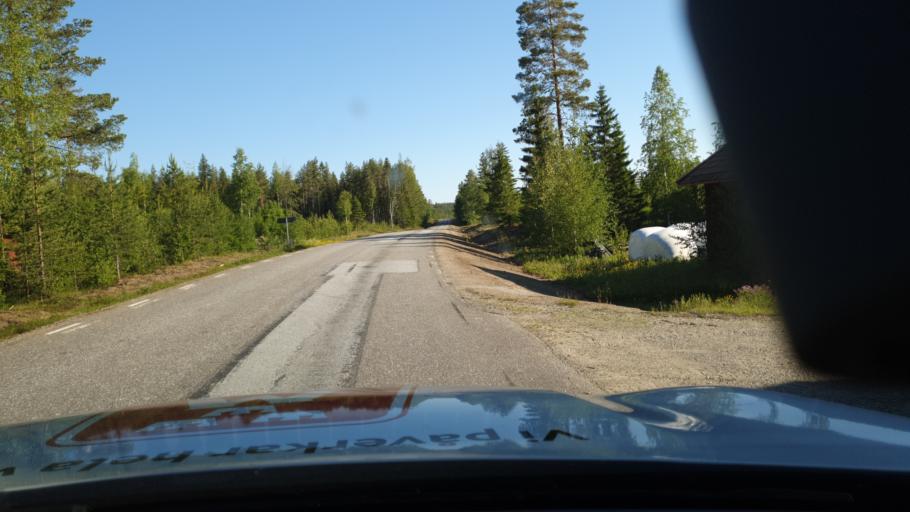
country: SE
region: Vaesterbotten
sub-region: Vannas Kommun
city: Vannasby
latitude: 64.0497
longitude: 20.0663
